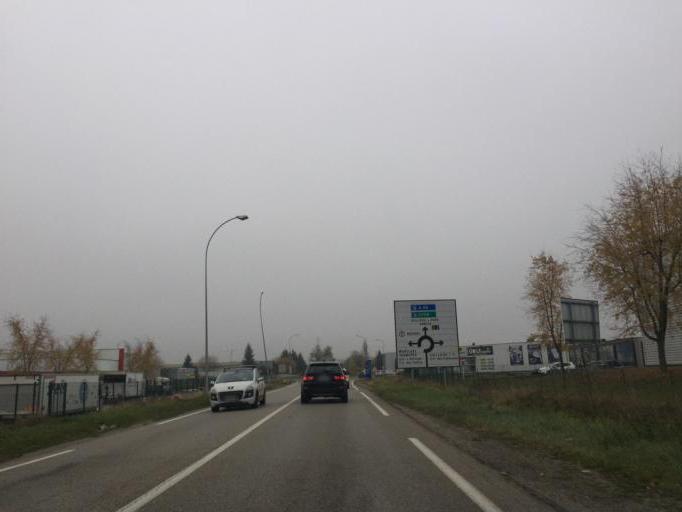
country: FR
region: Rhone-Alpes
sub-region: Departement de l'Ain
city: Mionnay
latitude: 45.8648
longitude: 4.9122
